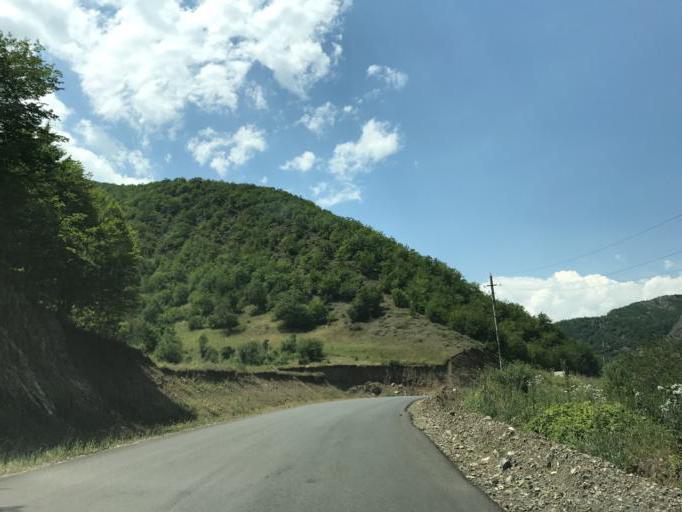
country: AZ
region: Kalbacar Rayonu
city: Kerbakhiar
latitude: 40.2278
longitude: 46.1638
